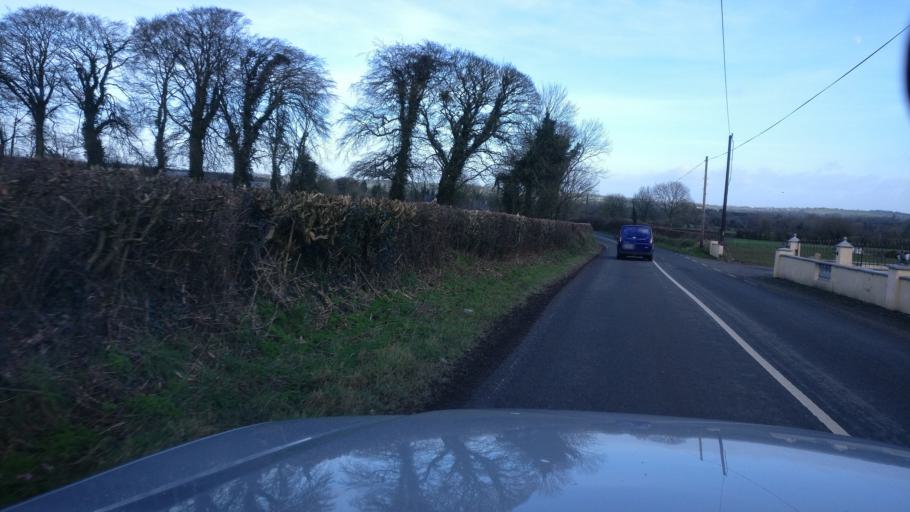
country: IE
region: Leinster
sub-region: Kilkenny
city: Castlecomer
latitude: 52.8401
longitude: -7.1880
